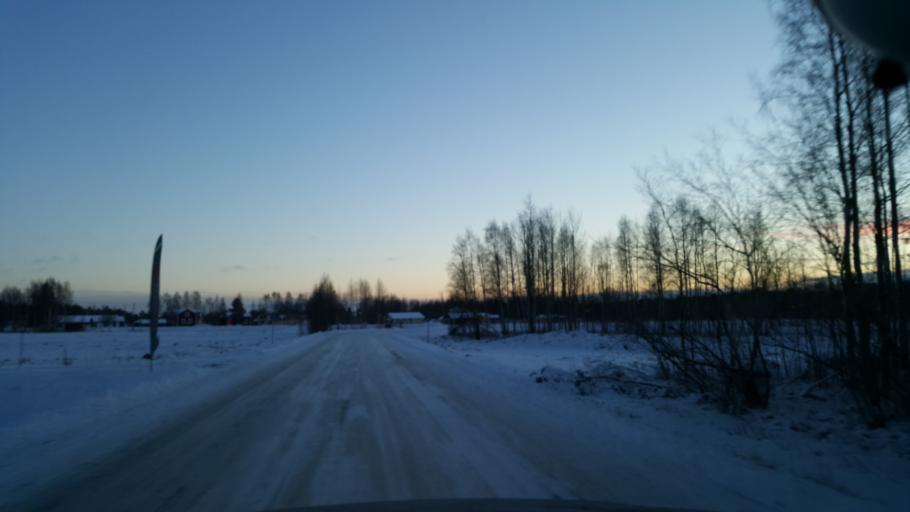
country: SE
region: Norrbotten
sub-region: Lulea Kommun
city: Sodra Sunderbyn
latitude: 65.5361
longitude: 21.9055
